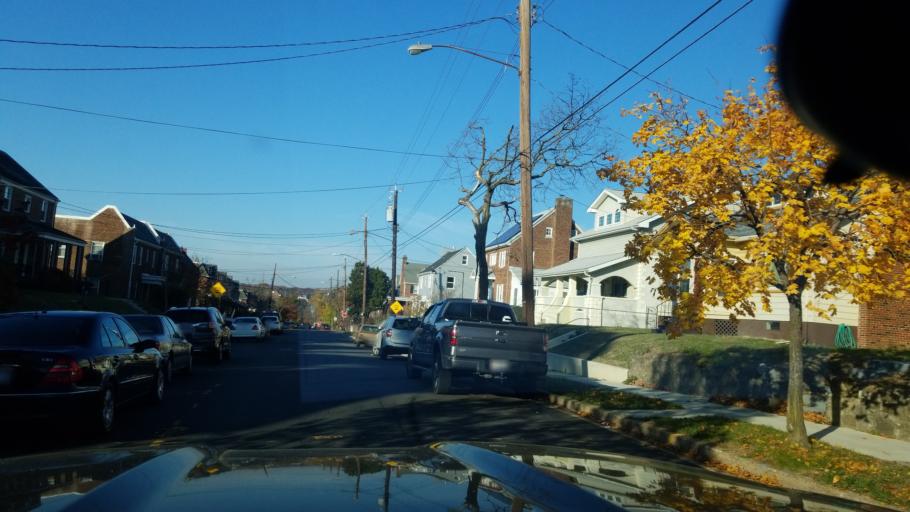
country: US
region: Maryland
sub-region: Montgomery County
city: Takoma Park
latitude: 38.9587
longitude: -77.0103
